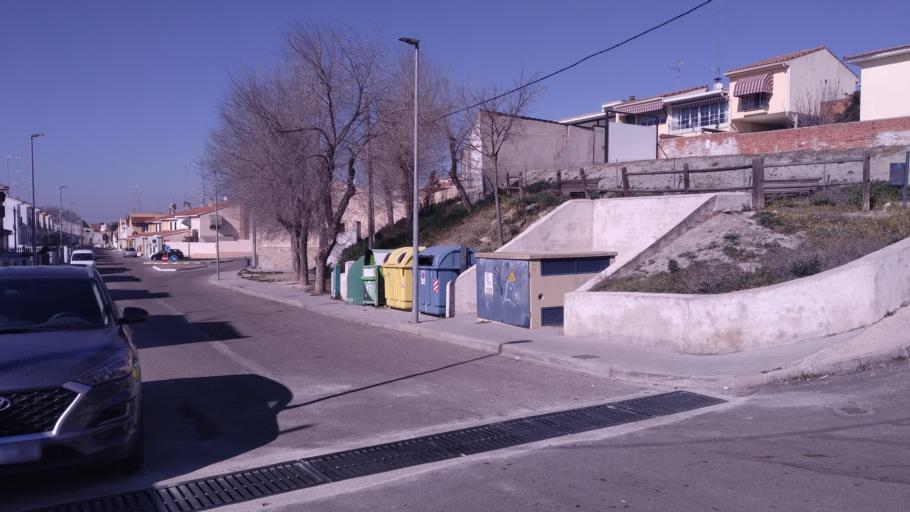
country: ES
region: Castille-La Mancha
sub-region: Province of Toledo
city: Esquivias
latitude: 40.1011
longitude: -3.7613
